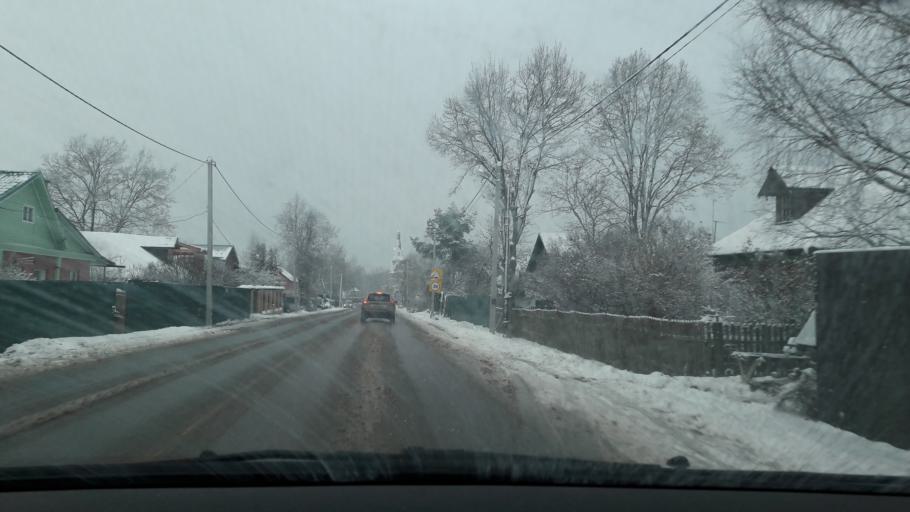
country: RU
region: Moskovskaya
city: Zvenigorod
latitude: 55.6435
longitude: 36.8340
